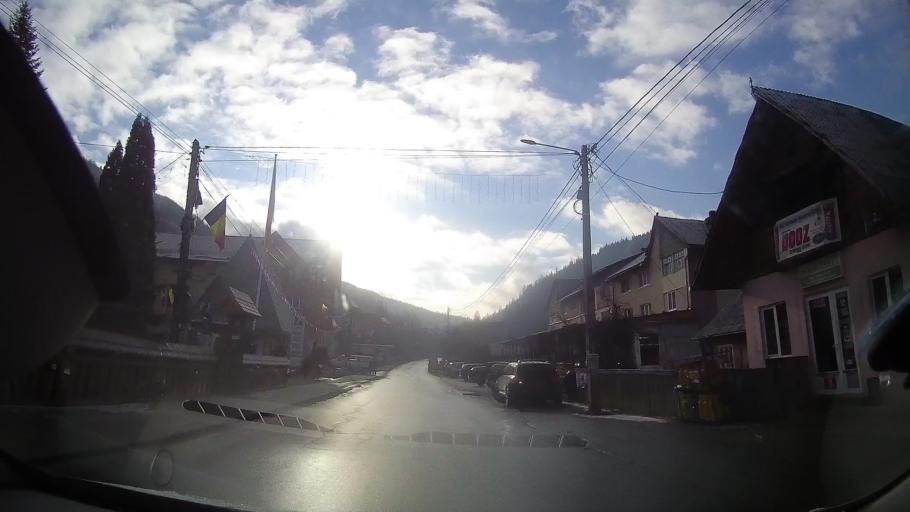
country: RO
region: Alba
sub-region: Comuna Albac
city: Albac
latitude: 46.4480
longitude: 22.9640
